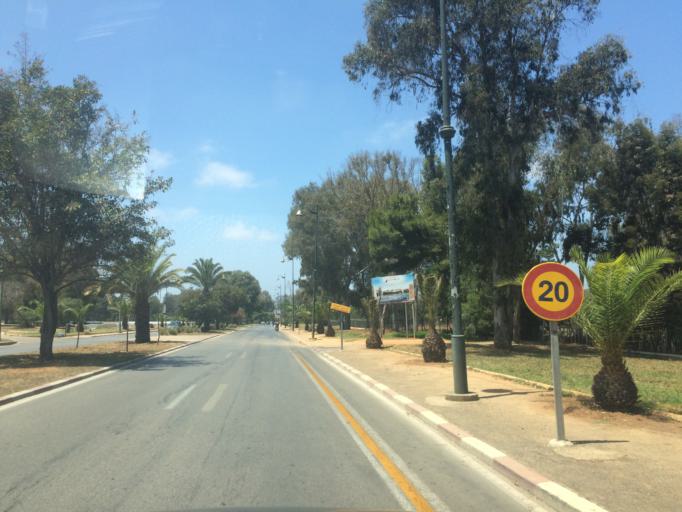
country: MA
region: Rabat-Sale-Zemmour-Zaer
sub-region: Rabat
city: Rabat
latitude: 33.9935
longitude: -6.8334
